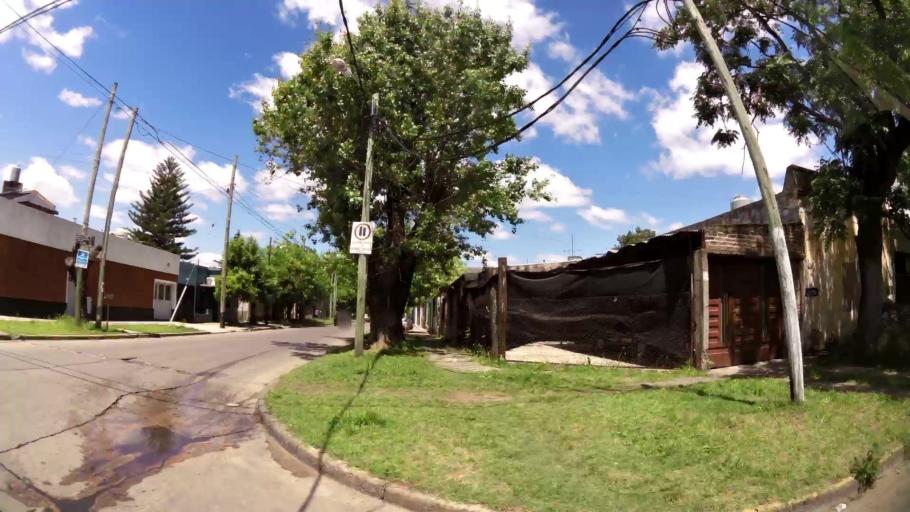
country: AR
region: Buenos Aires
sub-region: Partido de Lanus
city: Lanus
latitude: -34.7283
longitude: -58.4183
